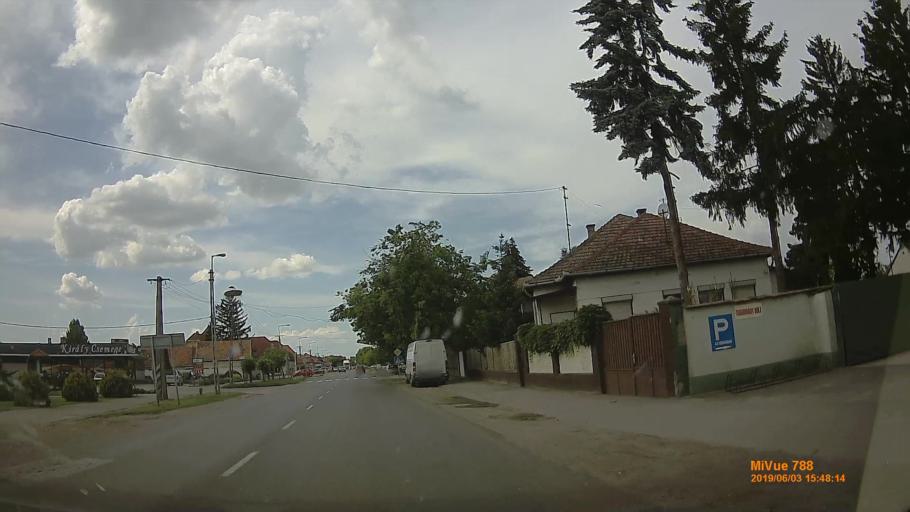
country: HU
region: Bacs-Kiskun
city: Akaszto
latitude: 46.6913
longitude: 19.2051
